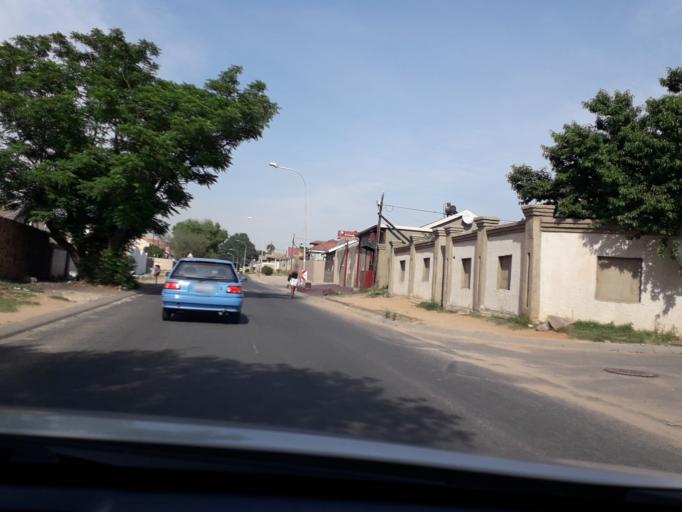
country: ZA
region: Gauteng
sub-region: City of Johannesburg Metropolitan Municipality
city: Modderfontein
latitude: -26.1186
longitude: 28.1053
